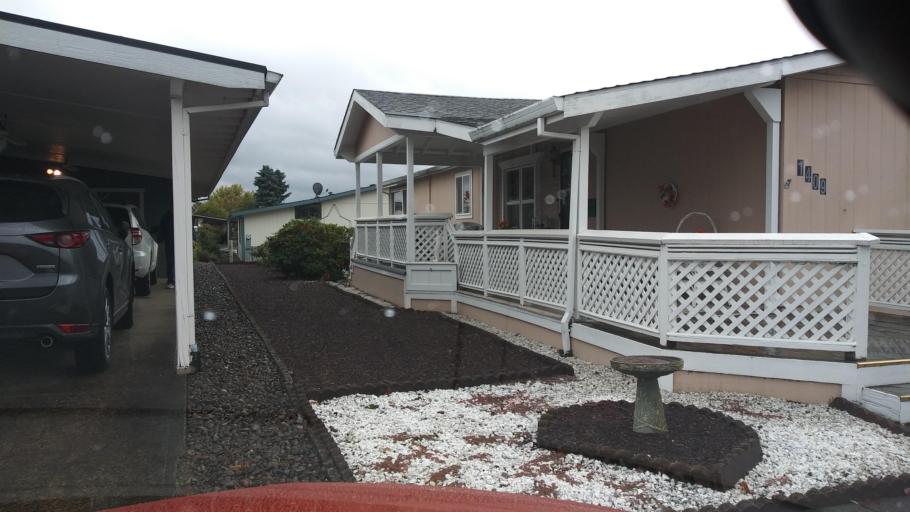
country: US
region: Oregon
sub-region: Washington County
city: Cornelius
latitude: 45.5129
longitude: -123.0741
